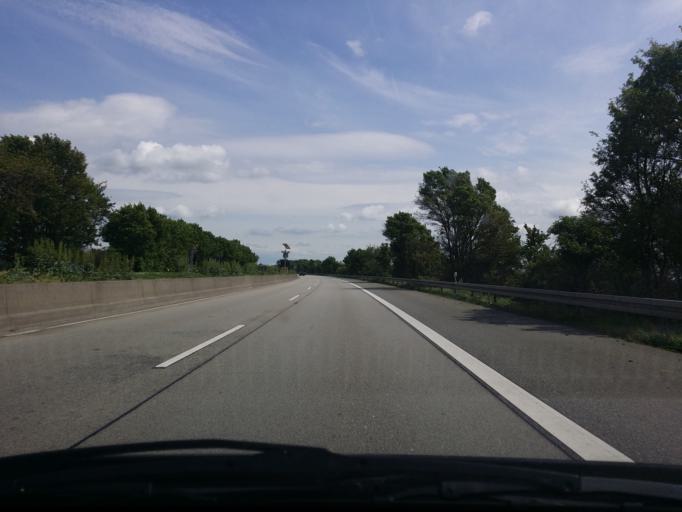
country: DE
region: Hesse
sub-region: Regierungsbezirk Darmstadt
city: Hochheim am Main
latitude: 50.0273
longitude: 8.3056
